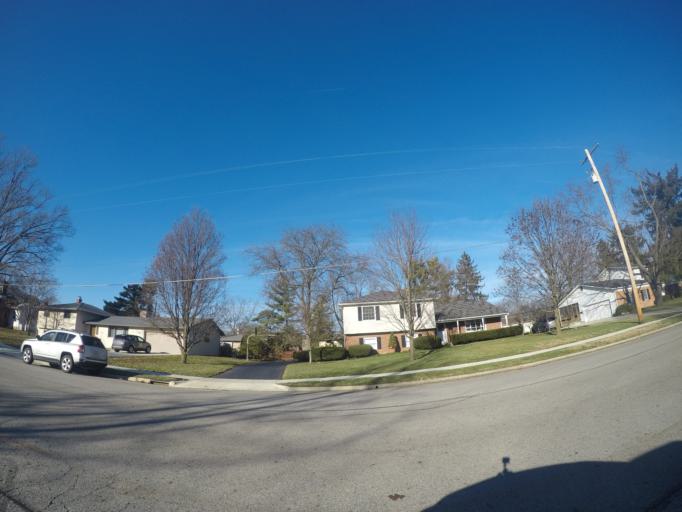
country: US
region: Ohio
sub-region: Franklin County
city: Upper Arlington
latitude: 40.0372
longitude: -83.0766
